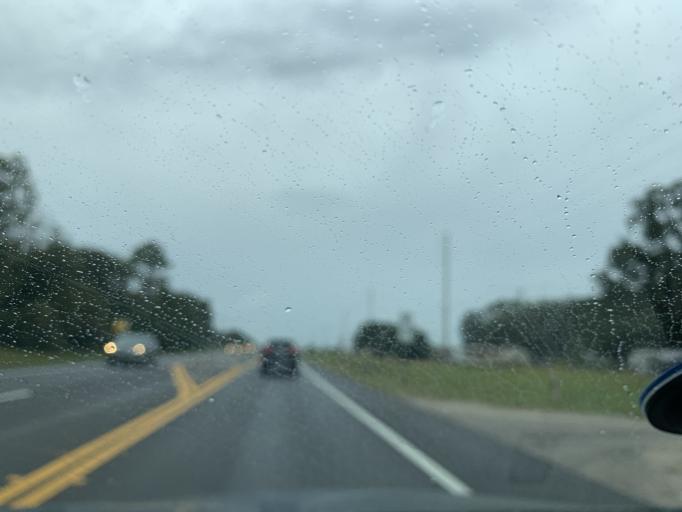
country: US
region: Florida
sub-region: Pasco County
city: Zephyrhills West
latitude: 28.2447
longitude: -82.2099
